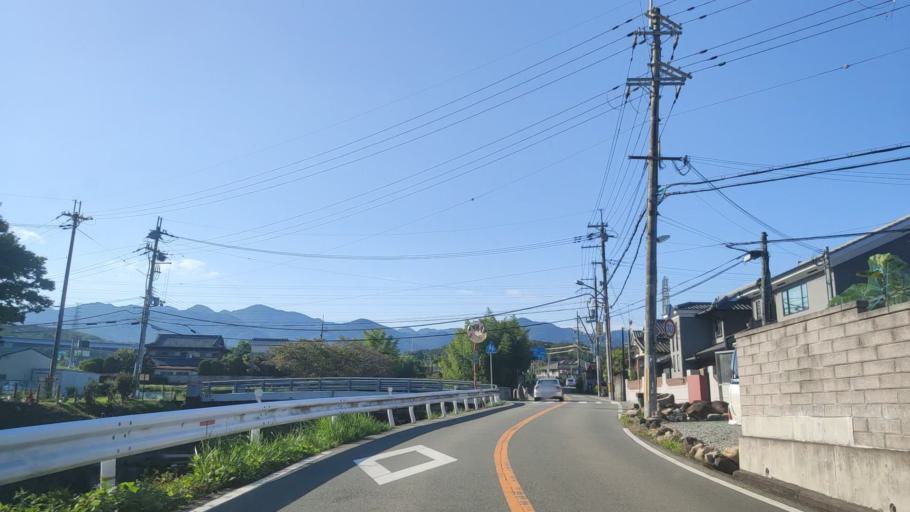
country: JP
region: Hyogo
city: Sandacho
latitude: 34.8225
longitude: 135.2467
